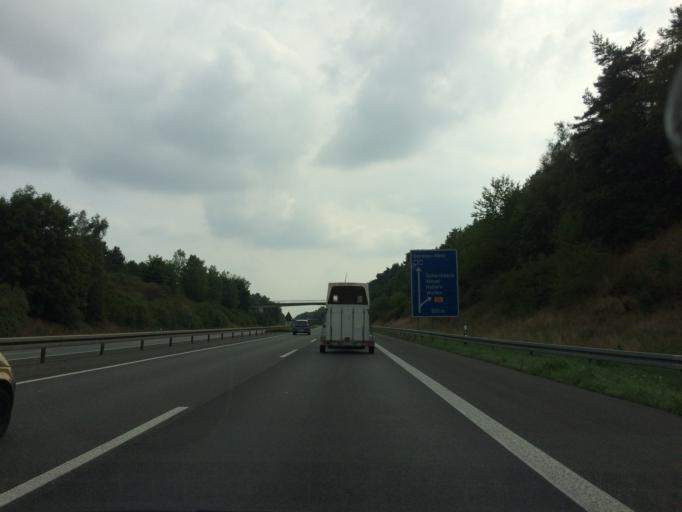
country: DE
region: North Rhine-Westphalia
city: Dorsten
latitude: 51.7073
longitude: 6.9267
